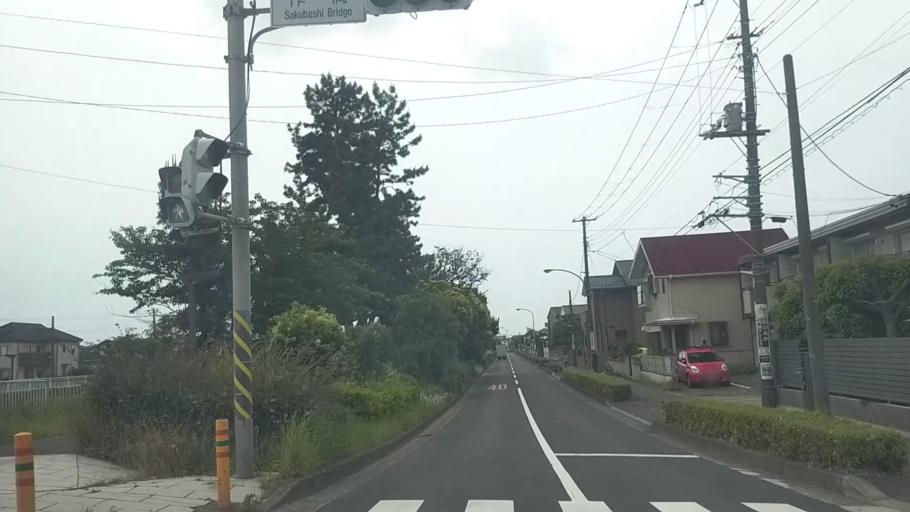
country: JP
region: Kanagawa
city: Fujisawa
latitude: 35.3257
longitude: 139.4627
